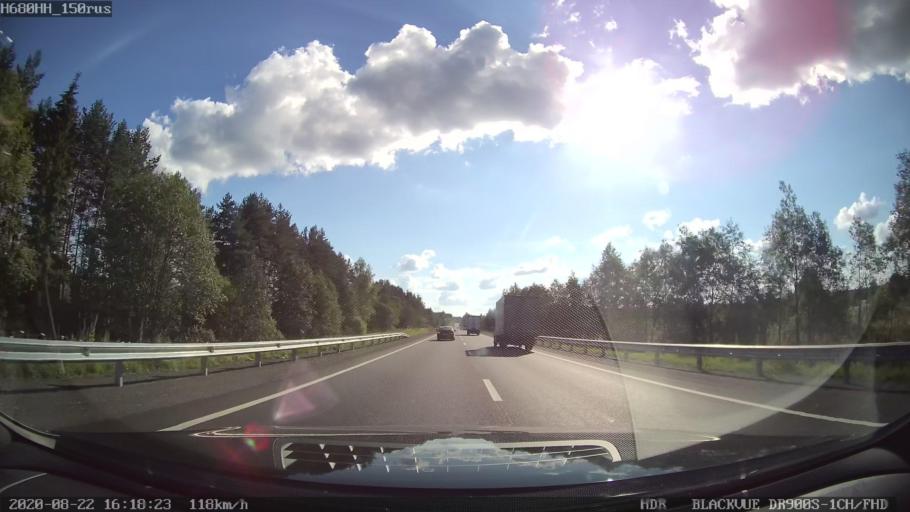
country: RU
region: Tverskaya
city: Rameshki
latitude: 57.4173
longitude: 36.1419
